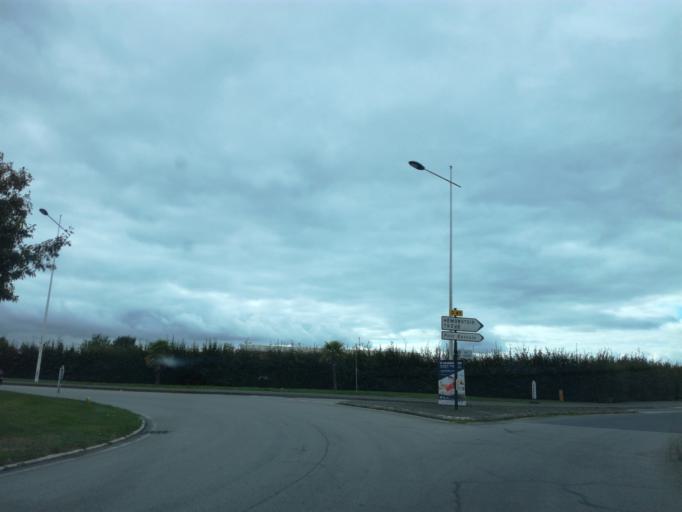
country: FR
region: Brittany
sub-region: Departement des Cotes-d'Armor
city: Loudeac
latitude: 48.1608
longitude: -2.7547
